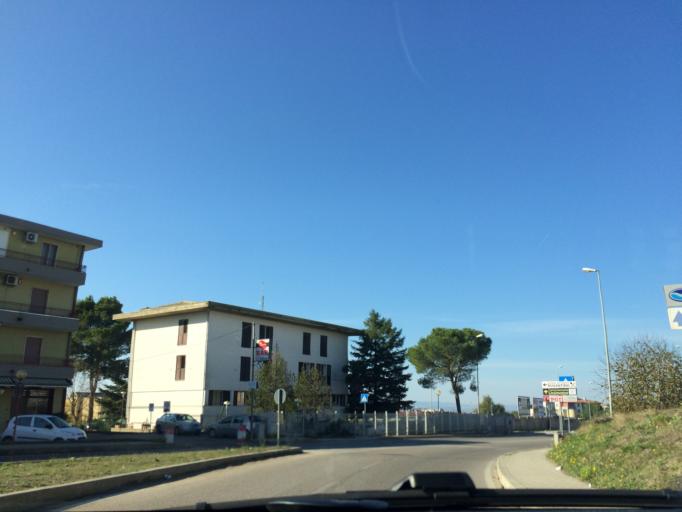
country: IT
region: Basilicate
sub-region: Provincia di Matera
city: Matera
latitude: 40.6819
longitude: 16.5808
